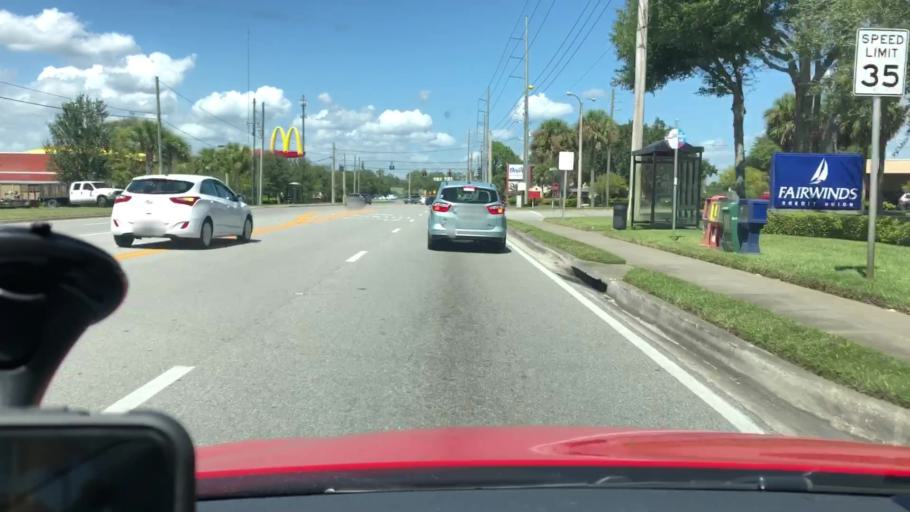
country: US
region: Florida
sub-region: Volusia County
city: Orange City
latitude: 28.9208
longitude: -81.2973
